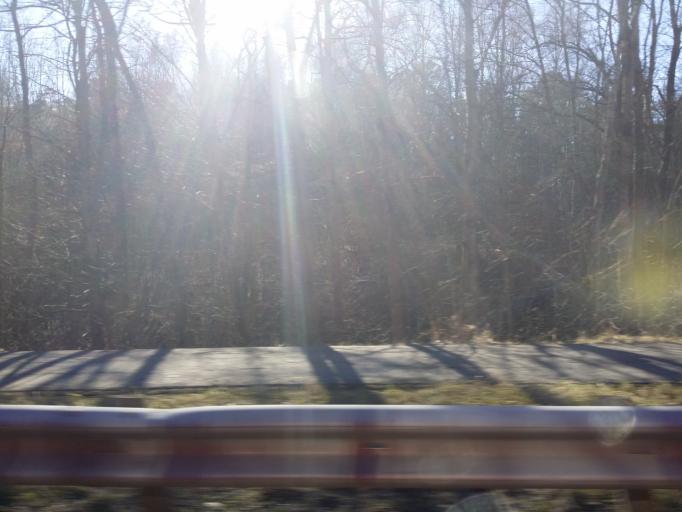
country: NO
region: Akershus
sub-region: Oppegard
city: Kolbotn
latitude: 59.8417
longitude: 10.7766
